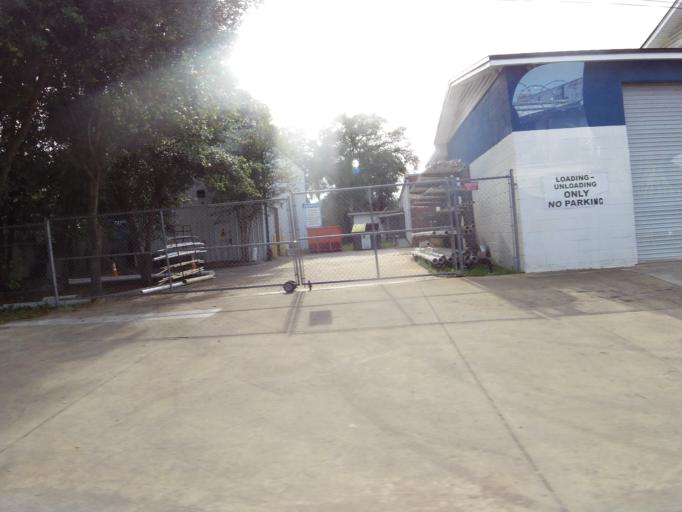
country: US
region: Florida
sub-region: Duval County
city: Jacksonville
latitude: 30.3331
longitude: -81.6010
